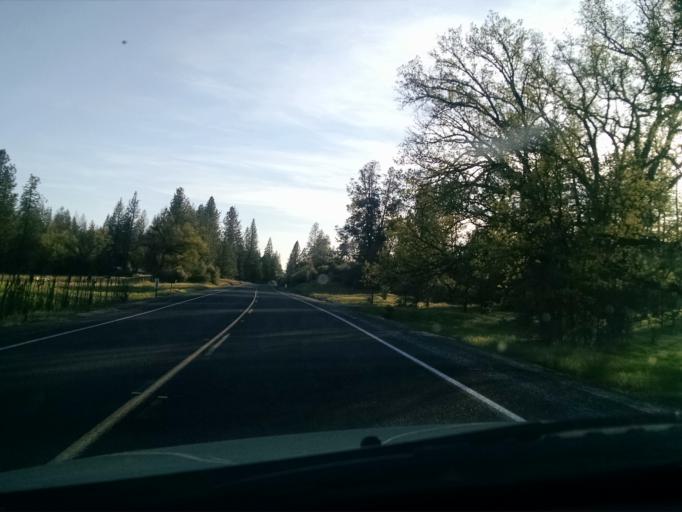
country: US
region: California
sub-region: Madera County
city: Ahwahnee
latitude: 37.4610
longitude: -119.7970
